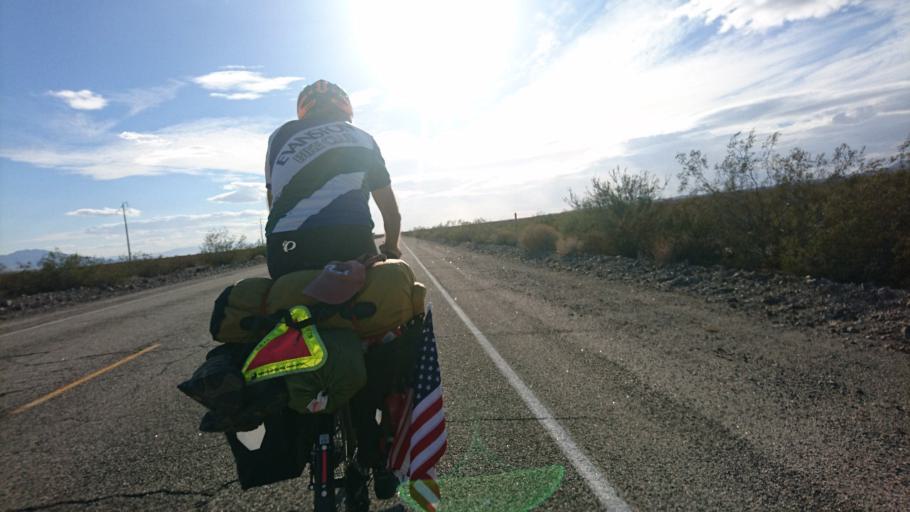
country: US
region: California
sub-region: San Bernardino County
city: Needles
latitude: 34.6855
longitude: -115.3190
